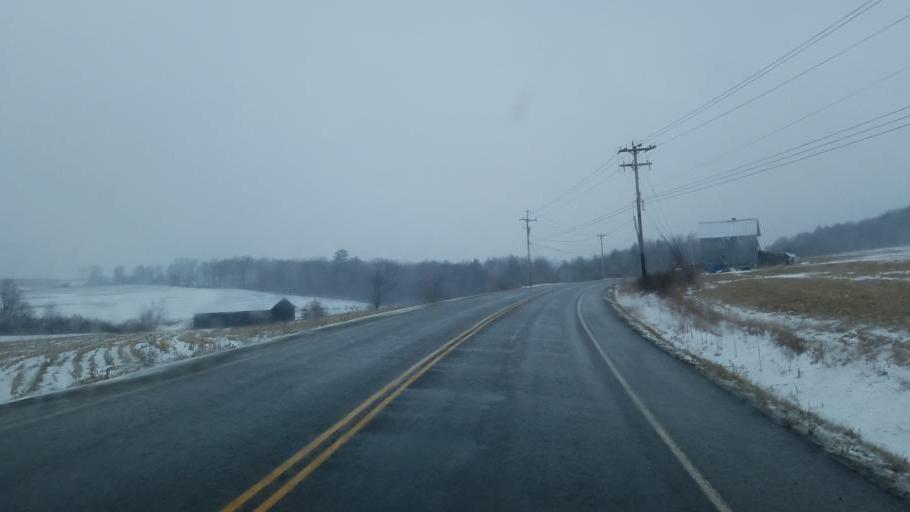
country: US
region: New York
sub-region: Steuben County
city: Canisteo
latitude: 42.1231
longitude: -77.5224
